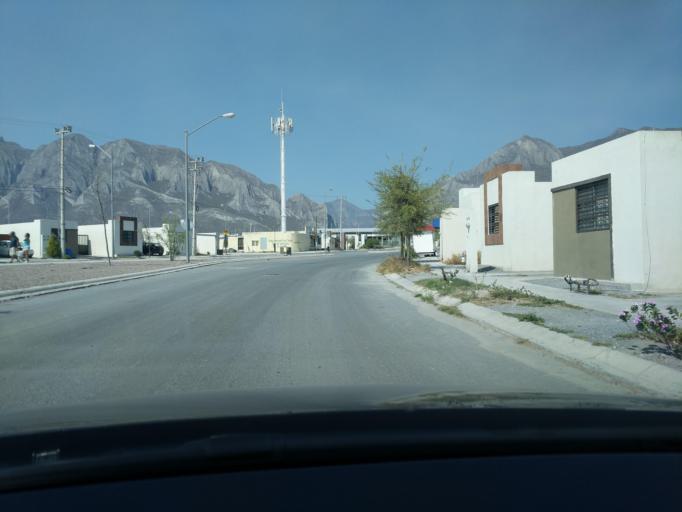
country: MX
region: Nuevo Leon
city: Garcia
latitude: 25.8163
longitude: -100.5398
